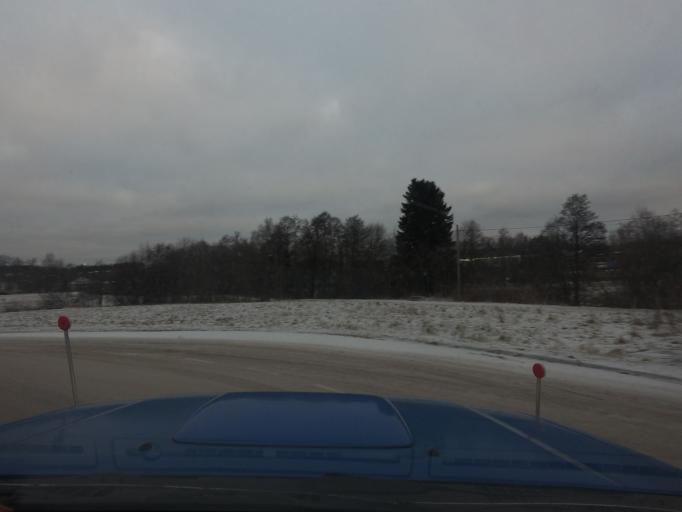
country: FI
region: Uusimaa
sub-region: Helsinki
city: Espoo
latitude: 60.2181
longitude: 24.6642
